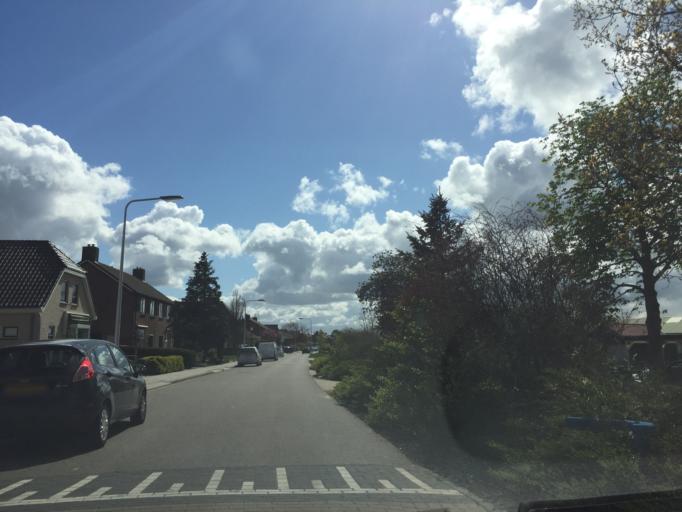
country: NL
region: South Holland
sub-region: Gemeente Kaag en Braassem
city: Oude Wetering
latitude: 52.2086
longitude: 4.6179
